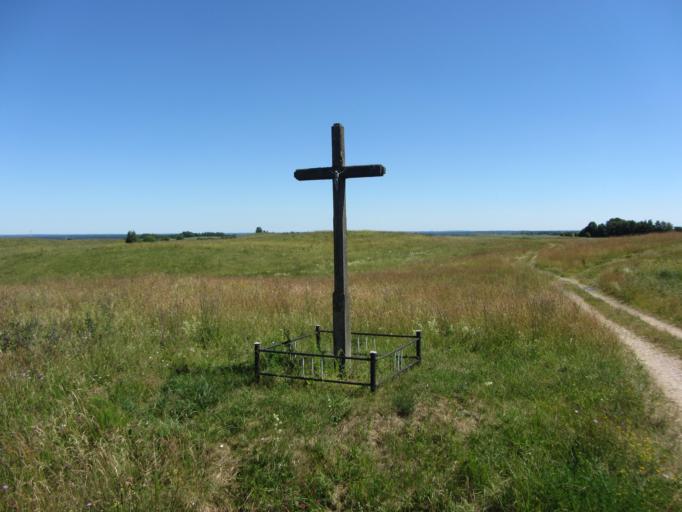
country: LT
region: Vilnius County
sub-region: Vilniaus Rajonas
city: Vievis
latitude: 54.7242
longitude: 24.7900
